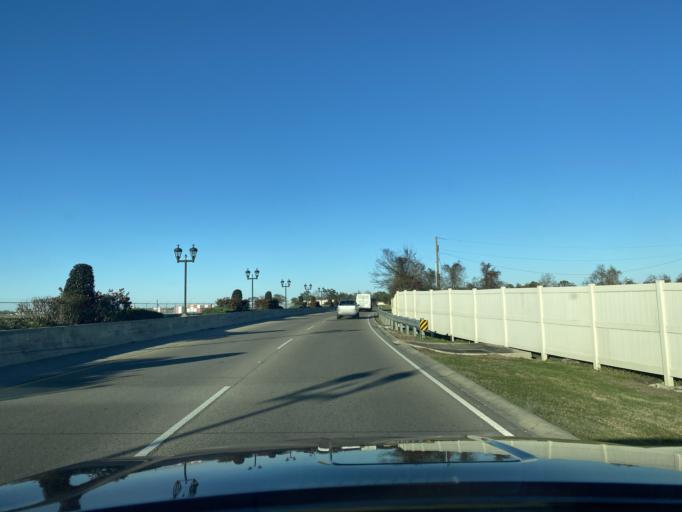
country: US
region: Louisiana
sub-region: Jefferson Parish
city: Kenner
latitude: 29.9862
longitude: -90.2492
